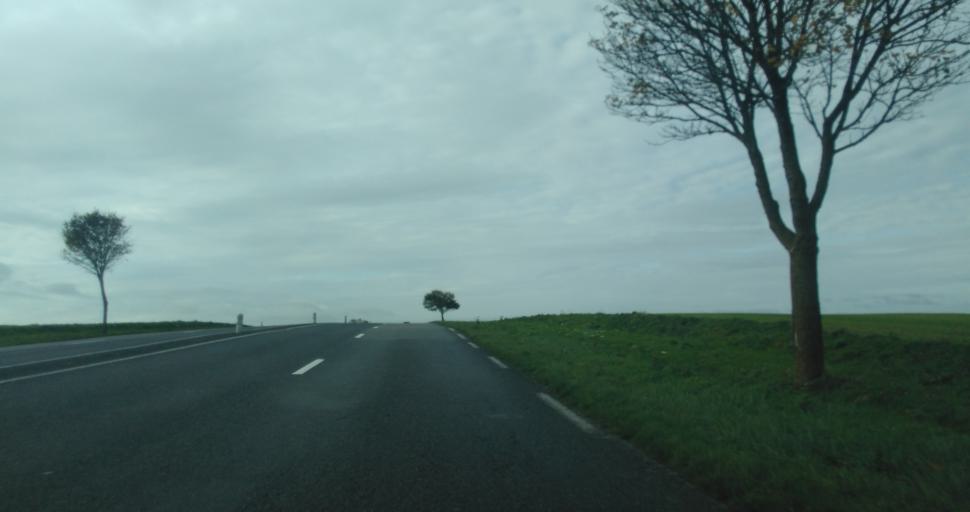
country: FR
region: Nord-Pas-de-Calais
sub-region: Departement du Pas-de-Calais
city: Auchy-les-Hesdin
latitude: 50.3830
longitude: 2.1362
